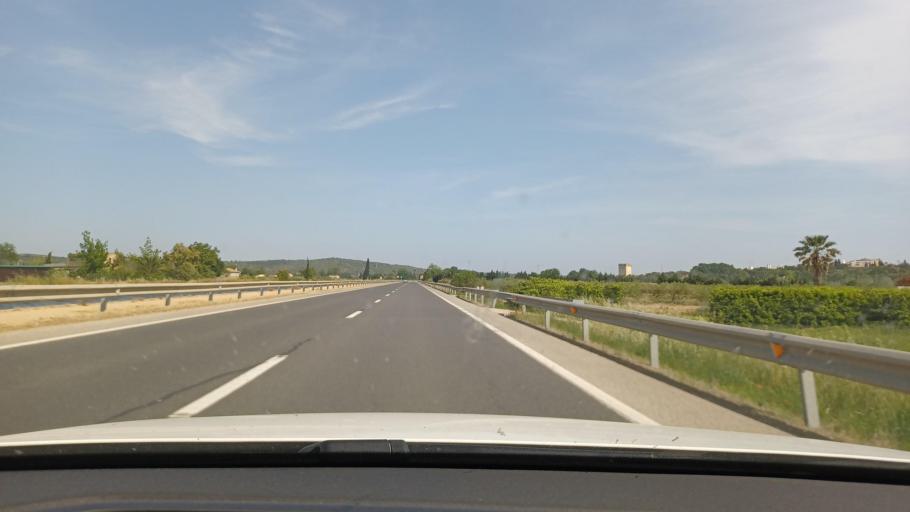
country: ES
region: Catalonia
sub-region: Provincia de Tarragona
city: Masdenverge
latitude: 40.7494
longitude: 0.5529
